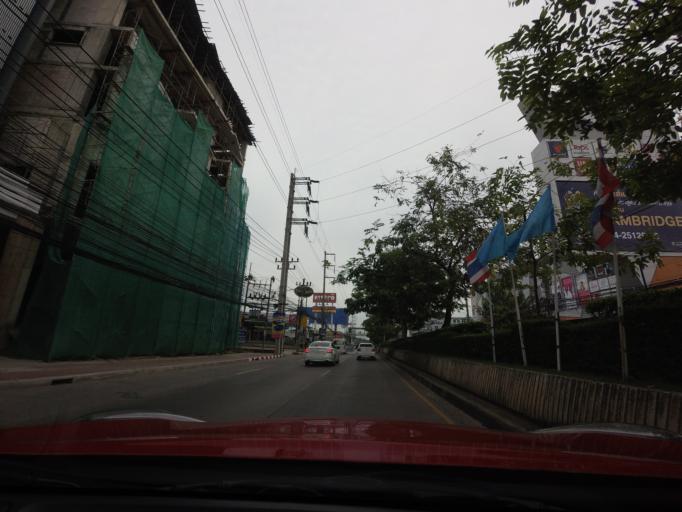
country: TH
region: Songkhla
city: Hat Yai
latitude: 6.9918
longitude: 100.4836
